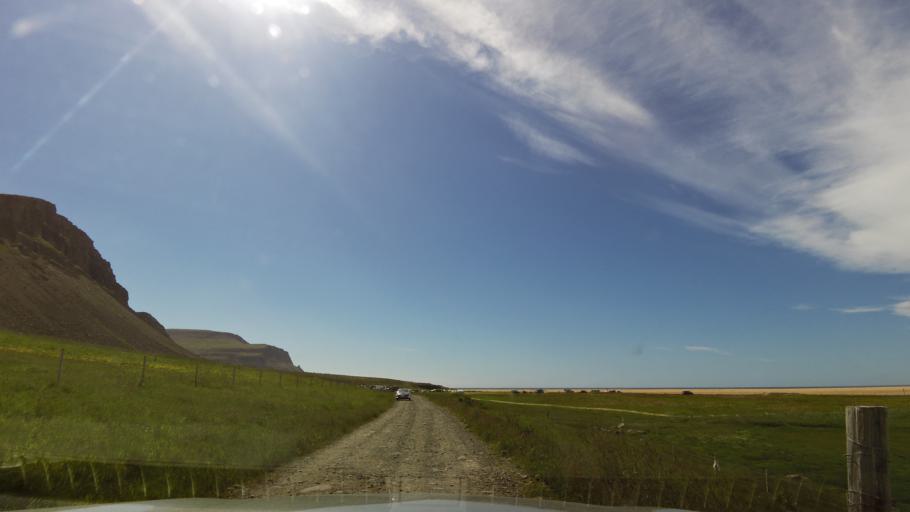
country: IS
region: West
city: Olafsvik
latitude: 65.4470
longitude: -23.9518
